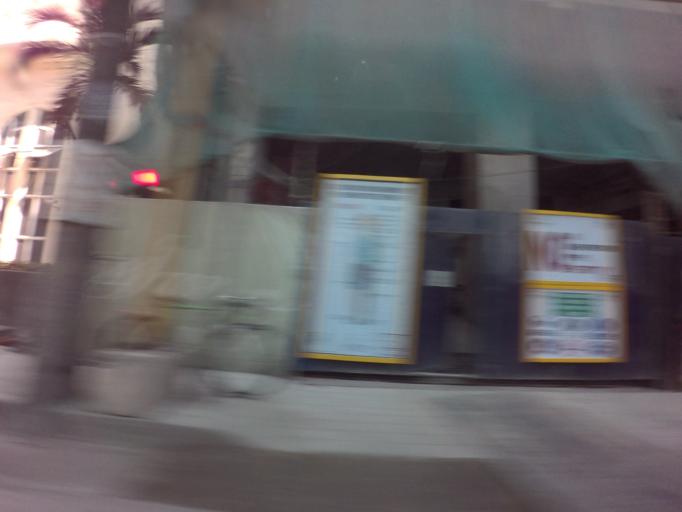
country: PH
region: Metro Manila
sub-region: Makati City
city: Makati City
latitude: 14.5594
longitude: 121.0095
